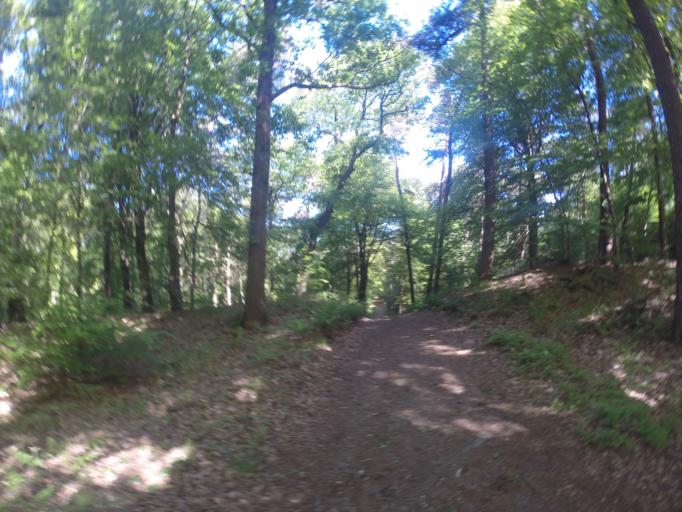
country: NL
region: Gelderland
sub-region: Gemeente Montferland
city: s-Heerenberg
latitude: 51.9146
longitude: 6.2274
